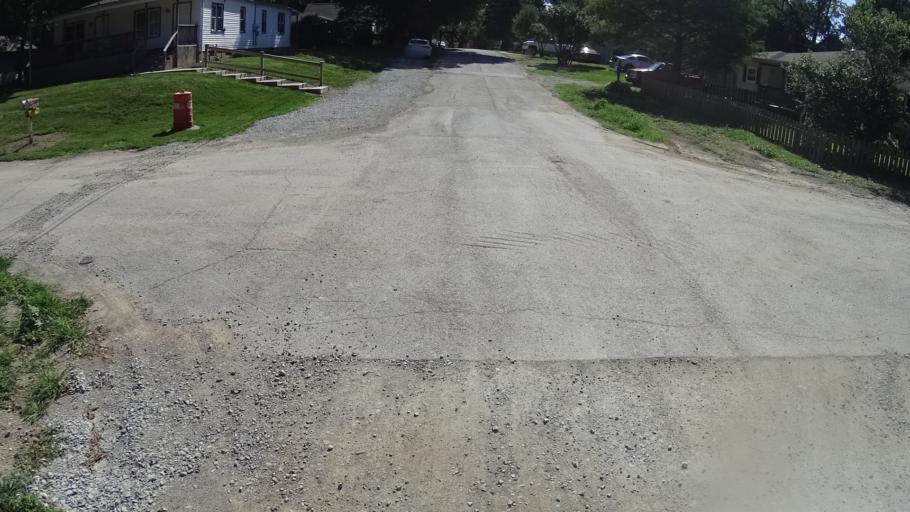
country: US
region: Indiana
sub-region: Madison County
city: Pendleton
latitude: 39.9940
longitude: -85.7466
